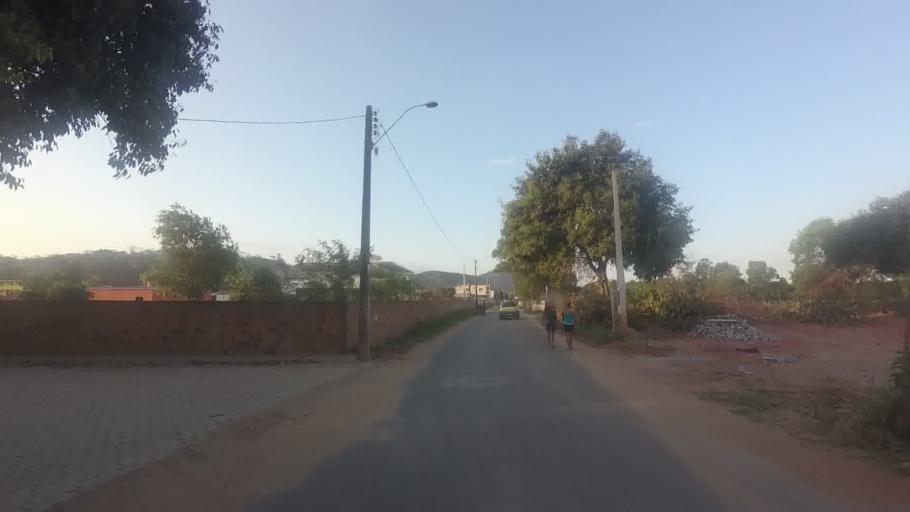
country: BR
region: Espirito Santo
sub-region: Piuma
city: Piuma
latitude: -20.8988
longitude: -40.7870
